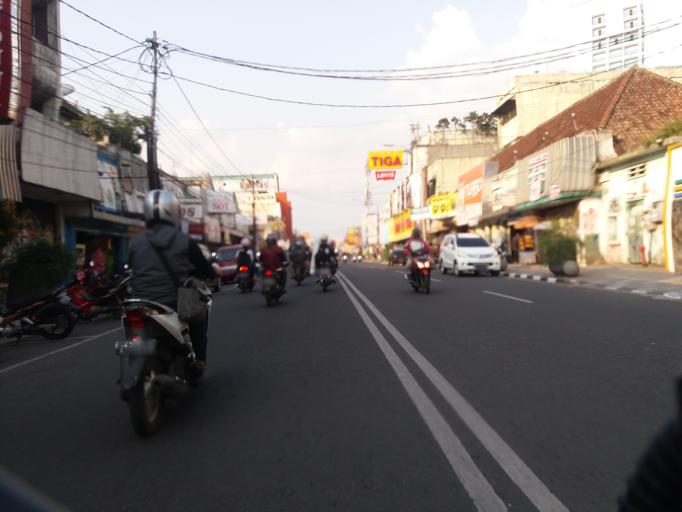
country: ID
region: West Java
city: Bandung
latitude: -6.9208
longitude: 107.6205
